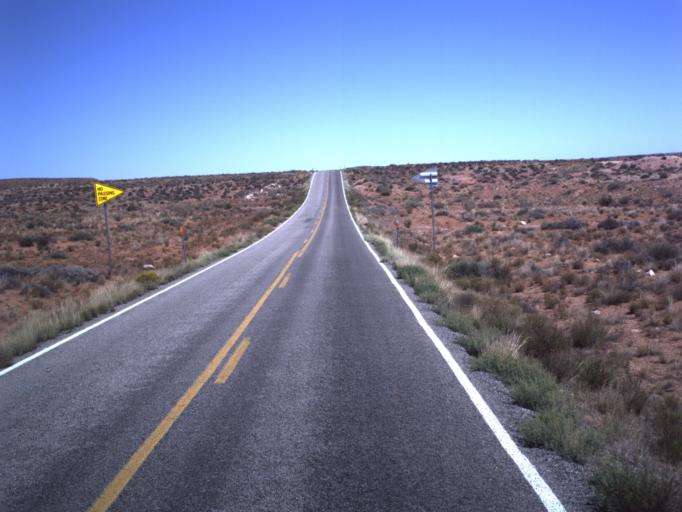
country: US
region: Arizona
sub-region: Navajo County
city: Kayenta
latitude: 37.1880
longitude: -109.9154
